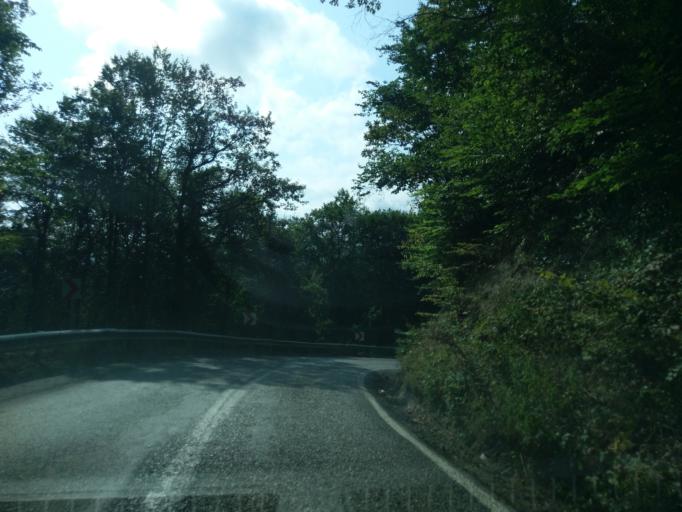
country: TR
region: Sinop
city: Ayancik
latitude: 41.8801
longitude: 34.5190
